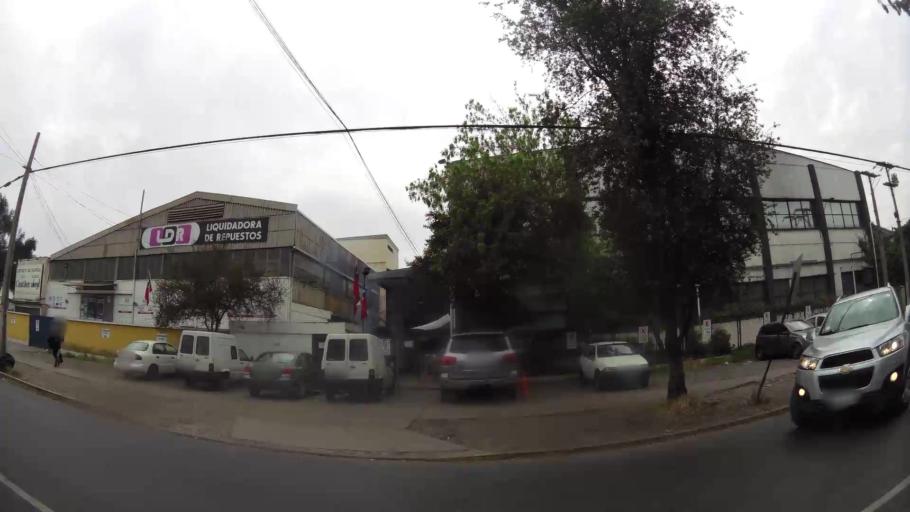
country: CL
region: Santiago Metropolitan
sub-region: Provincia de Santiago
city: Villa Presidente Frei, Nunoa, Santiago, Chile
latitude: -33.4833
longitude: -70.6062
